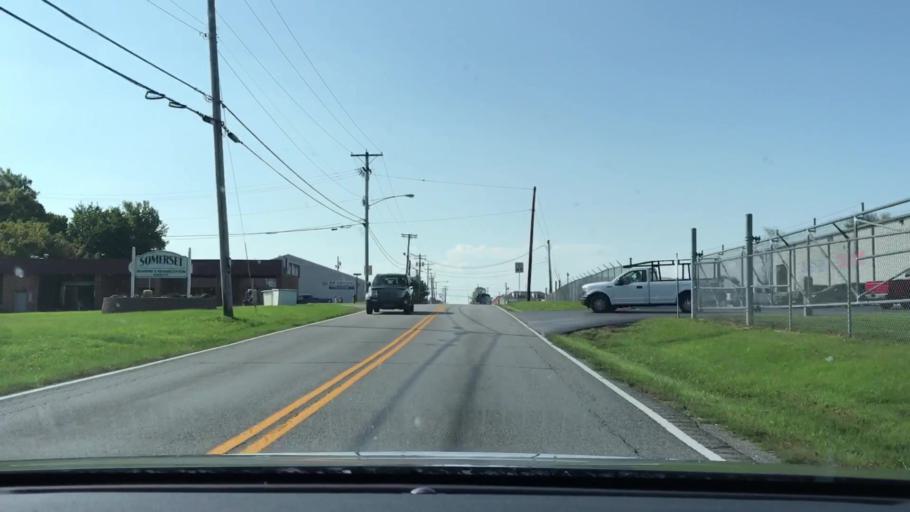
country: US
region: Kentucky
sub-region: Pulaski County
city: Somerset
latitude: 37.0727
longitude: -84.6160
